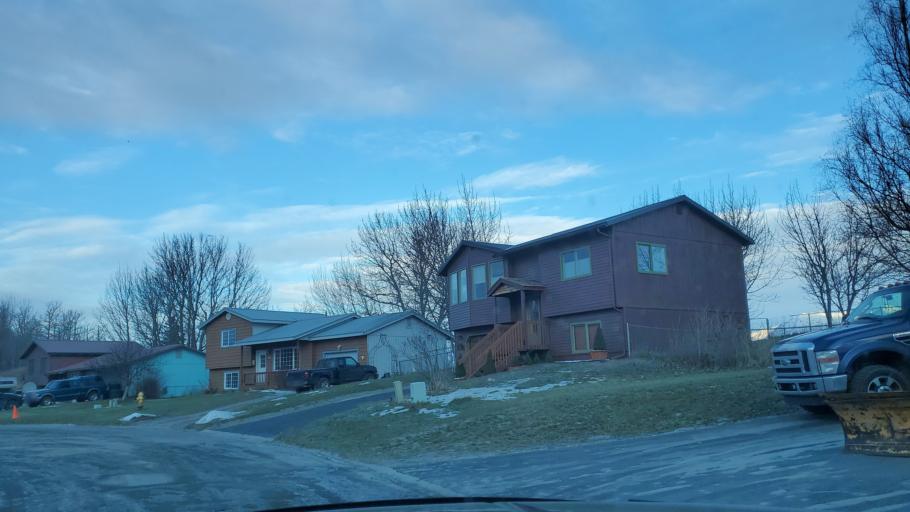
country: US
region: Alaska
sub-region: Matanuska-Susitna Borough
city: Palmer
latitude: 61.6154
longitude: -149.1040
